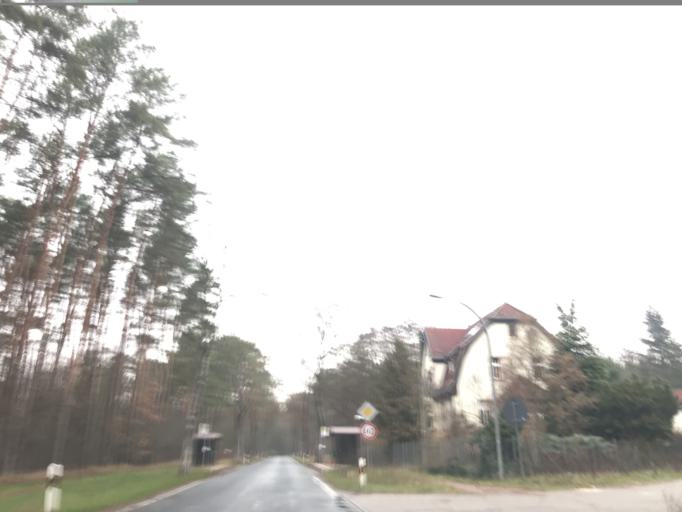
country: DE
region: Brandenburg
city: Brieselang
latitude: 52.6621
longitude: 12.9816
